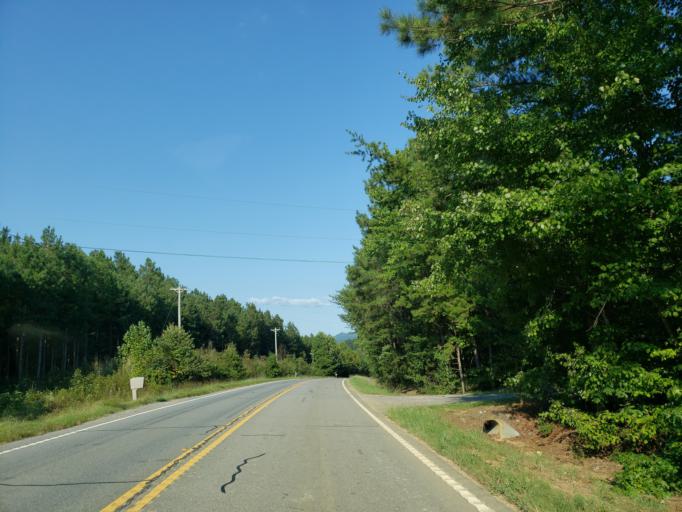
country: US
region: Tennessee
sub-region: Bradley County
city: Wildwood Lake
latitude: 34.9414
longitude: -84.7891
